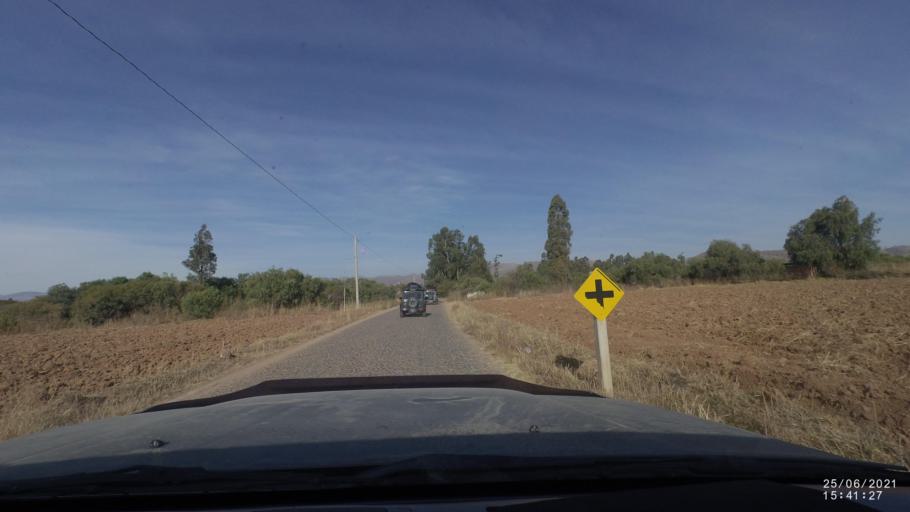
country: BO
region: Cochabamba
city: Cliza
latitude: -17.6343
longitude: -65.9183
